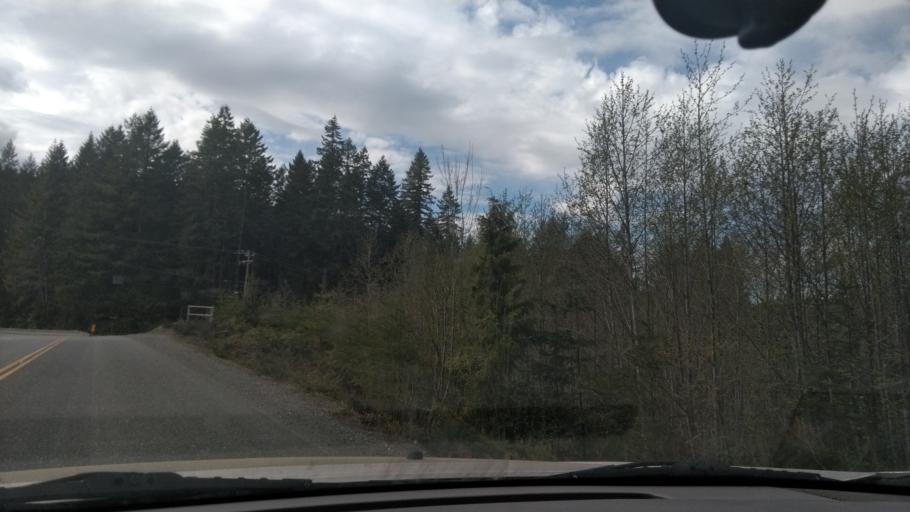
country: CA
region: British Columbia
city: Campbell River
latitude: 49.9981
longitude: -125.3780
